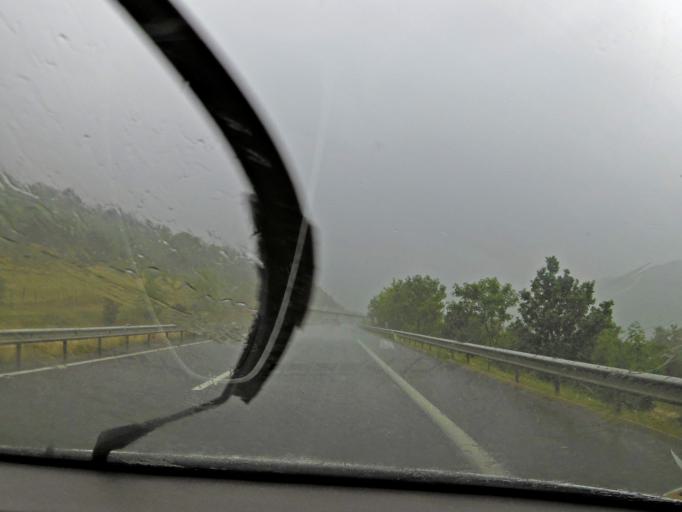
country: FR
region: Auvergne
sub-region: Departement du Cantal
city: Massiac
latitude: 45.2529
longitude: 3.2040
